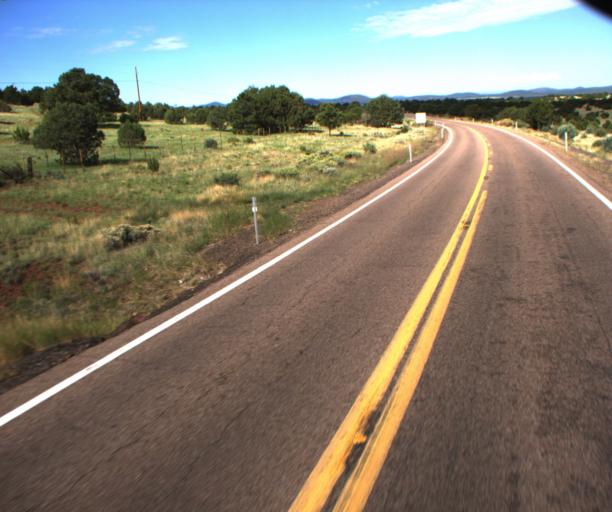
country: US
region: Arizona
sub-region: Apache County
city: Saint Johns
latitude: 34.2686
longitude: -109.5948
